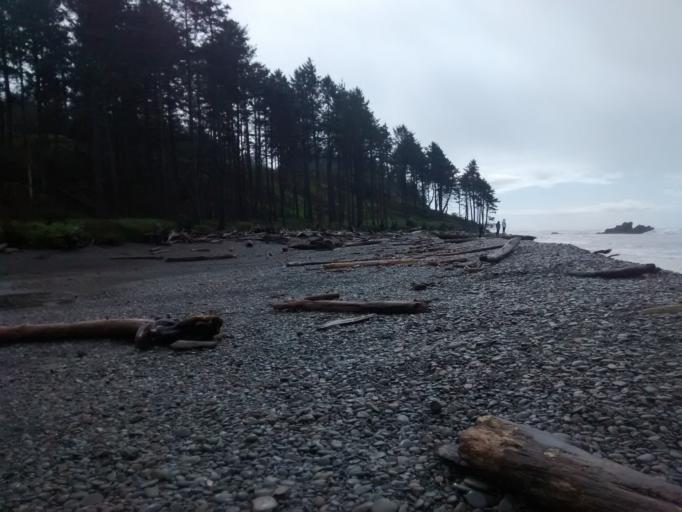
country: US
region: Washington
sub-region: Clallam County
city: Forks
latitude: 47.7110
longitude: -124.4157
